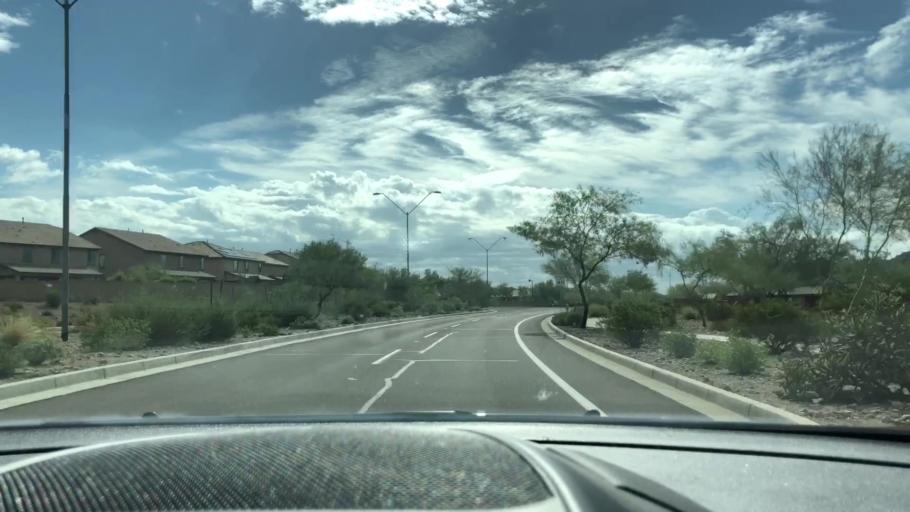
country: US
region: Arizona
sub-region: Maricopa County
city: Sun City West
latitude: 33.7365
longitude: -112.2555
